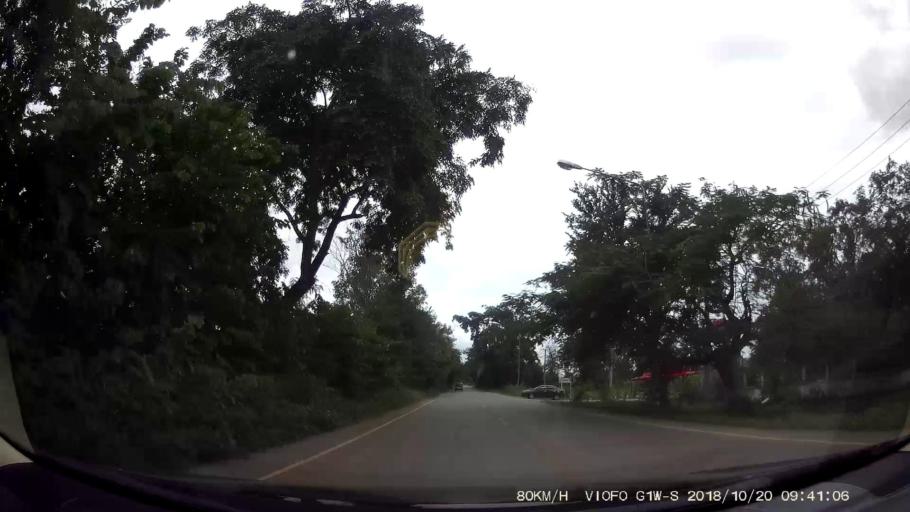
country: TH
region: Chaiyaphum
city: Khon San
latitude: 16.4498
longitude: 101.9585
